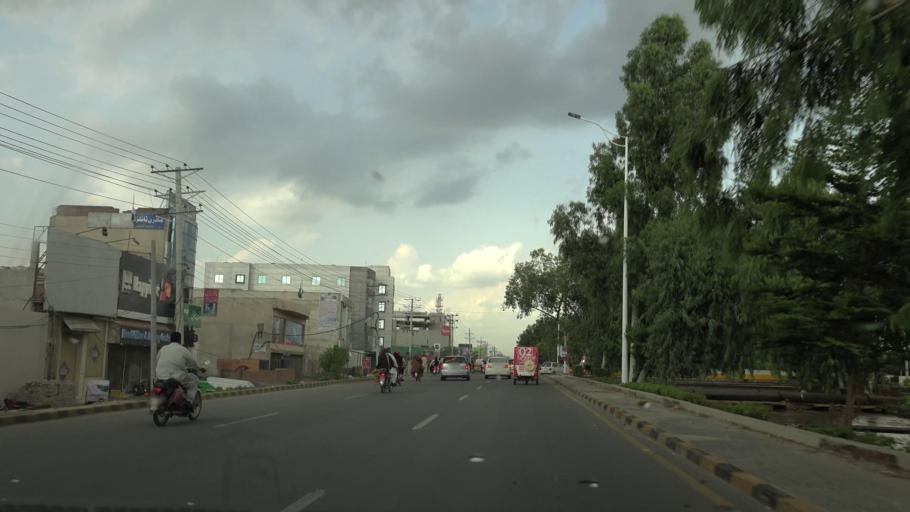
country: PK
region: Punjab
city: Faisalabad
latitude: 31.4380
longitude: 73.1305
